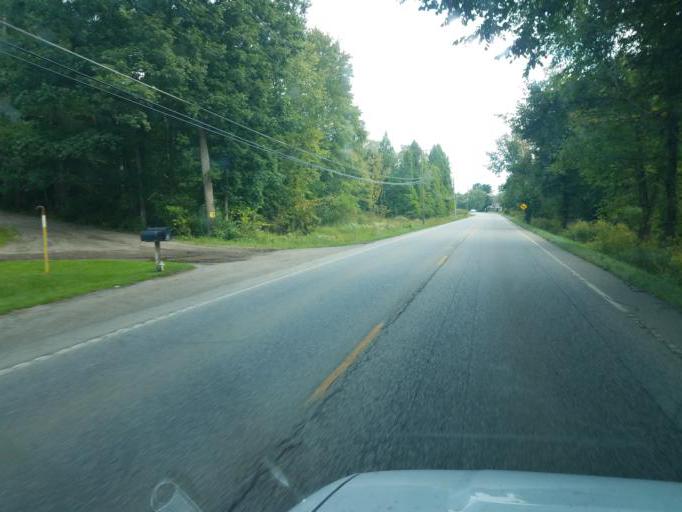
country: US
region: Ohio
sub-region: Carroll County
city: Lake Mohawk
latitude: 40.7009
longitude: -81.2710
